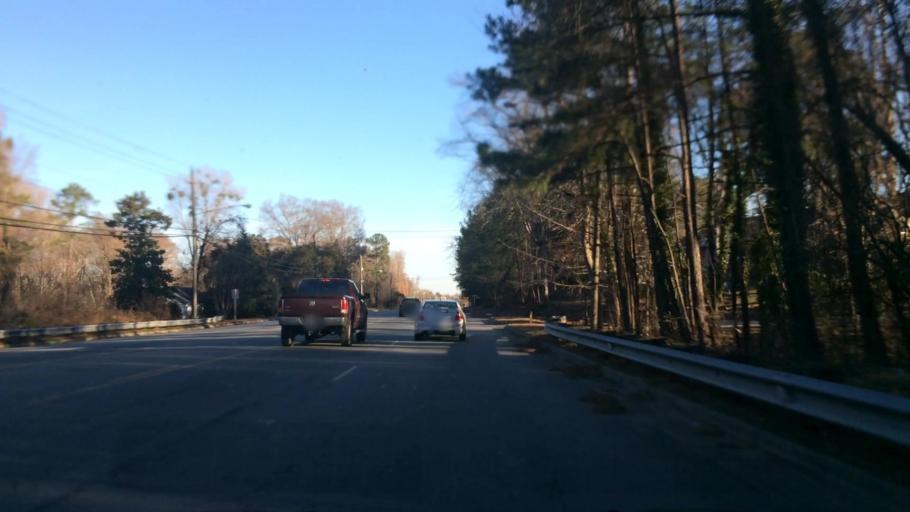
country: US
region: North Carolina
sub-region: Pitt County
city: Greenville
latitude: 35.5863
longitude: -77.3794
